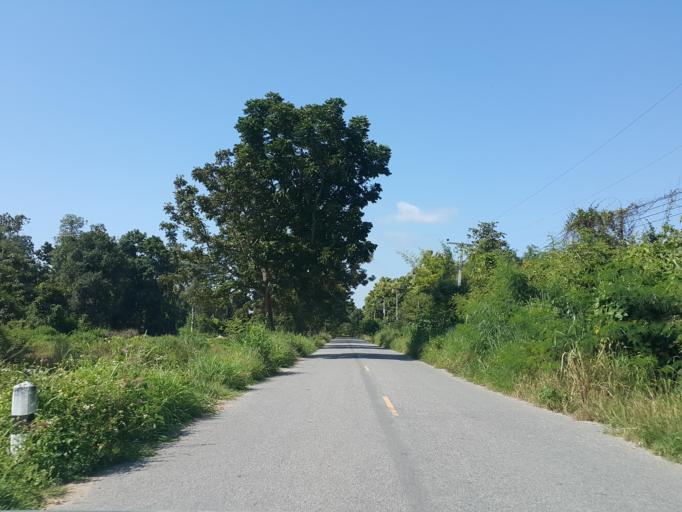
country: TH
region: Chiang Mai
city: Mae On
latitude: 18.7803
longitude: 99.1820
